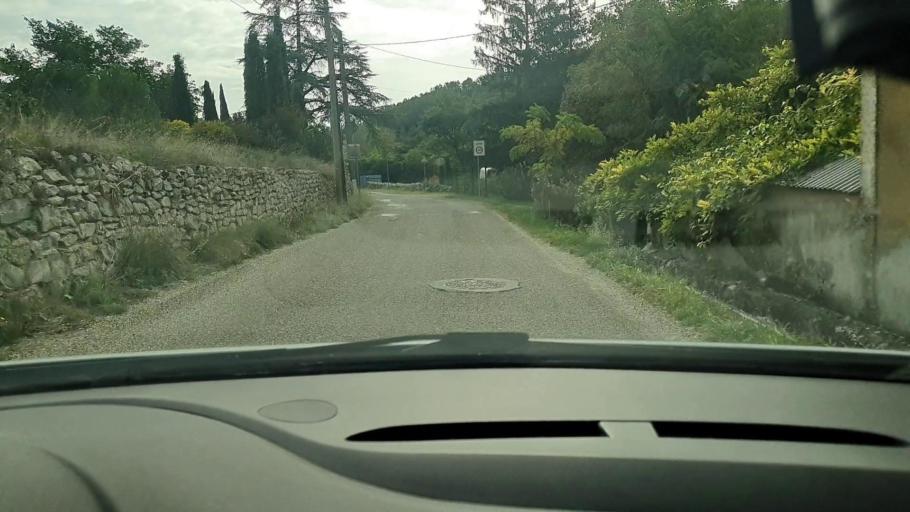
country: FR
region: Languedoc-Roussillon
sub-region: Departement du Gard
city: Montaren-et-Saint-Mediers
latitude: 44.0847
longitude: 4.3635
